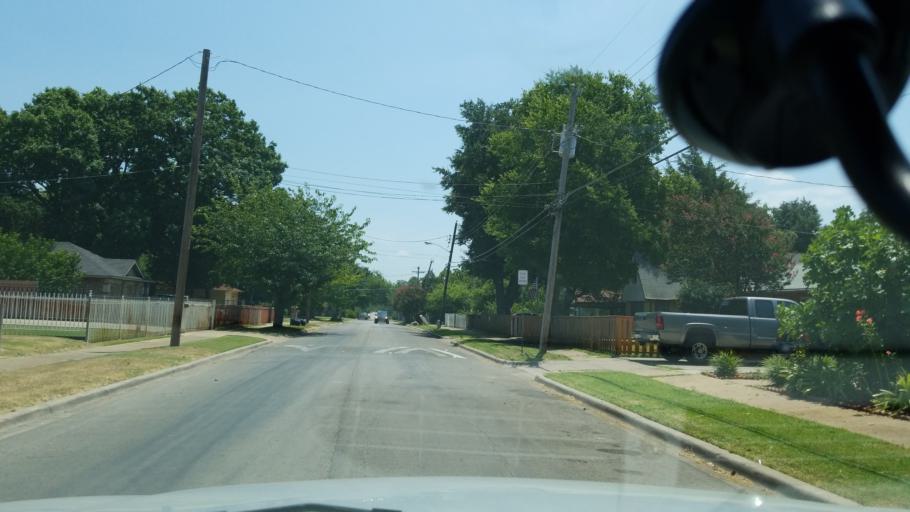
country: US
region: Texas
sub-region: Dallas County
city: Cockrell Hill
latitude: 32.7185
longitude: -96.8639
